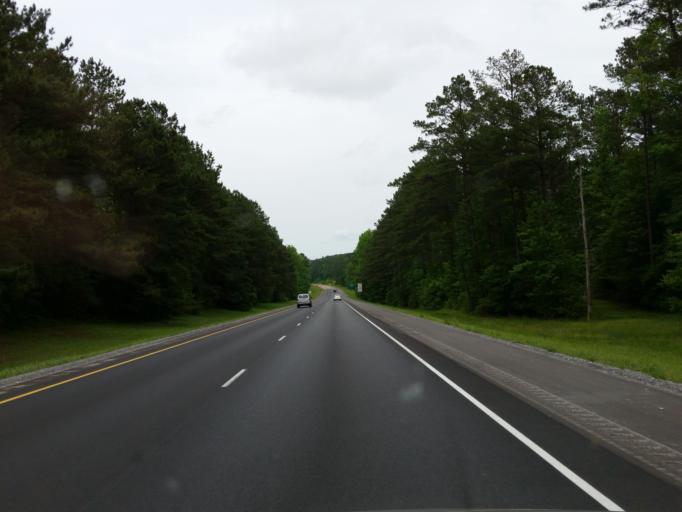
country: US
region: Mississippi
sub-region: Jones County
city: Sharon
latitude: 31.9702
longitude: -88.9610
